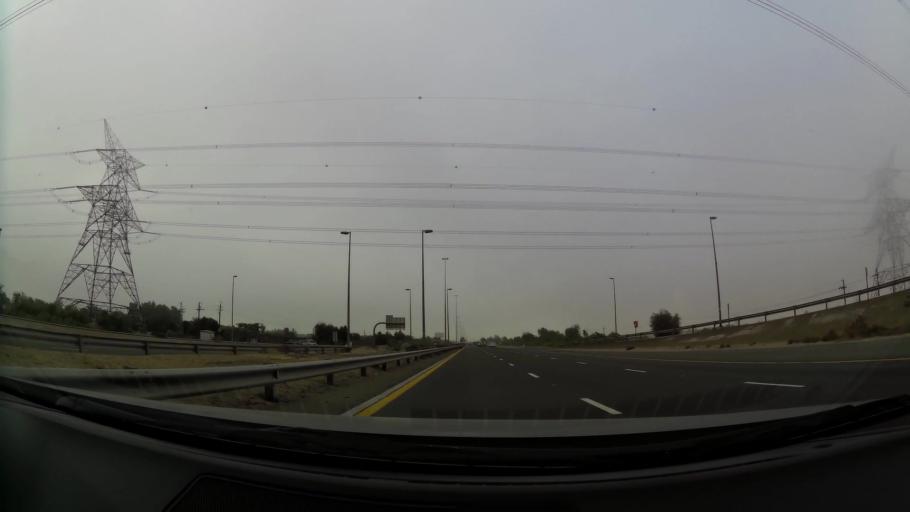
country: AE
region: Dubai
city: Dubai
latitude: 25.0845
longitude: 55.3945
